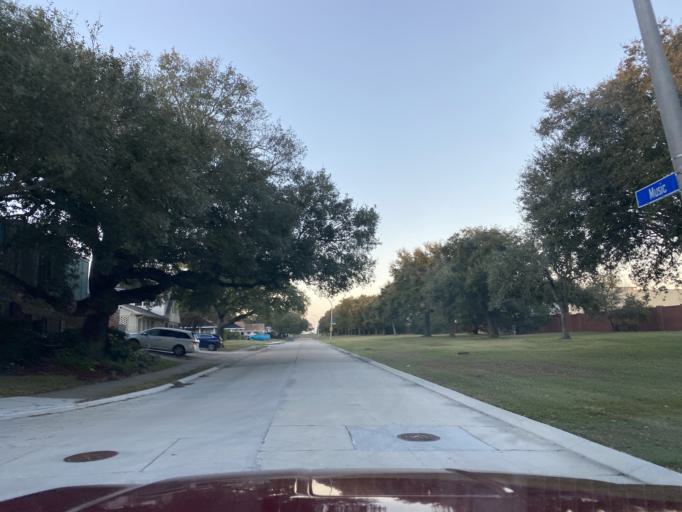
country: US
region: Louisiana
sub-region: Orleans Parish
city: New Orleans
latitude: 30.0267
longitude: -90.0550
